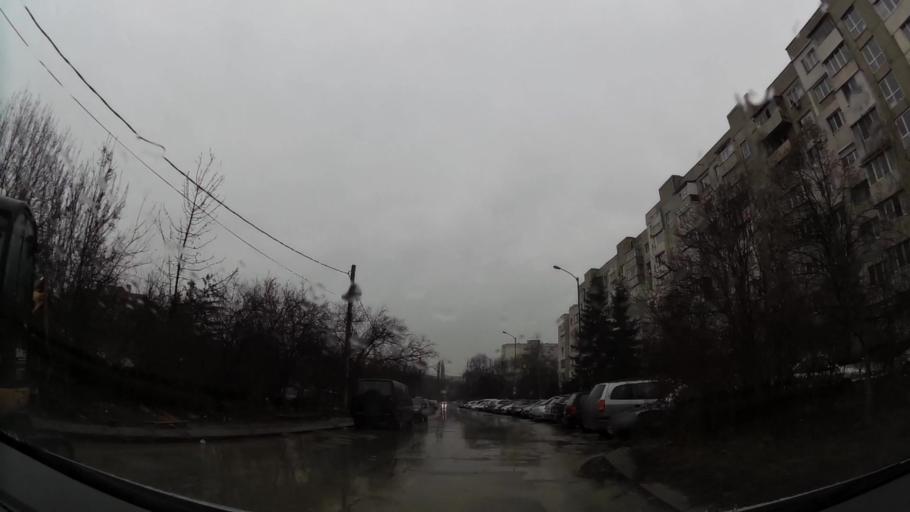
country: BG
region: Sofia-Capital
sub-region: Stolichna Obshtina
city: Sofia
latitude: 42.6562
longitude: 23.3641
